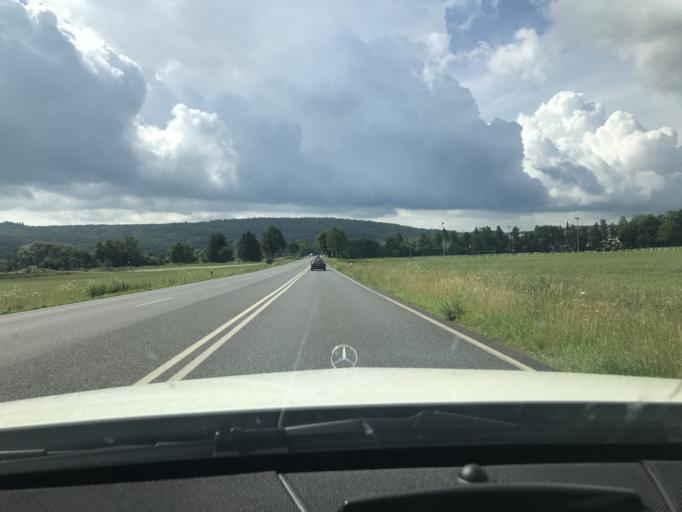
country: DE
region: Hesse
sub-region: Regierungsbezirk Kassel
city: Bad Hersfeld
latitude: 50.9104
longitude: 9.7476
